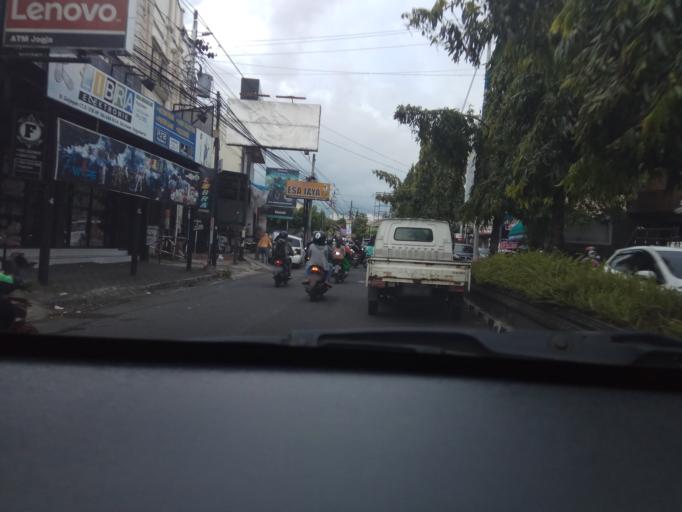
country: ID
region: Daerah Istimewa Yogyakarta
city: Yogyakarta
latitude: -7.7644
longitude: 110.3930
